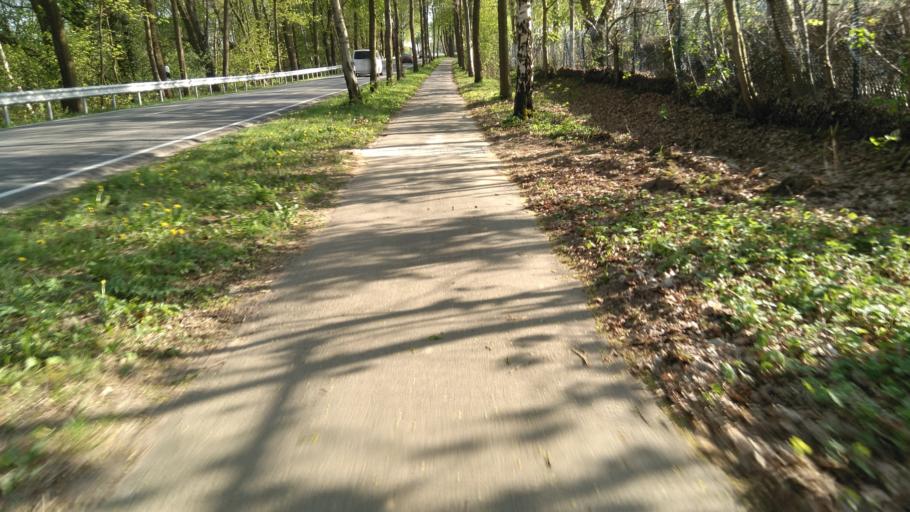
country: DE
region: Lower Saxony
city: Buxtehude
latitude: 53.4482
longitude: 9.6941
